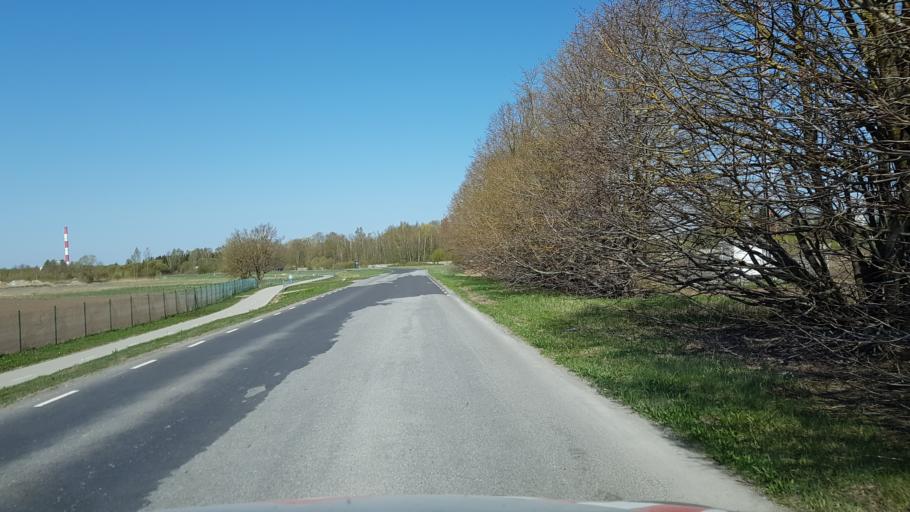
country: EE
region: Harju
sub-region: Joelaehtme vald
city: Loo
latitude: 59.4247
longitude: 24.9444
